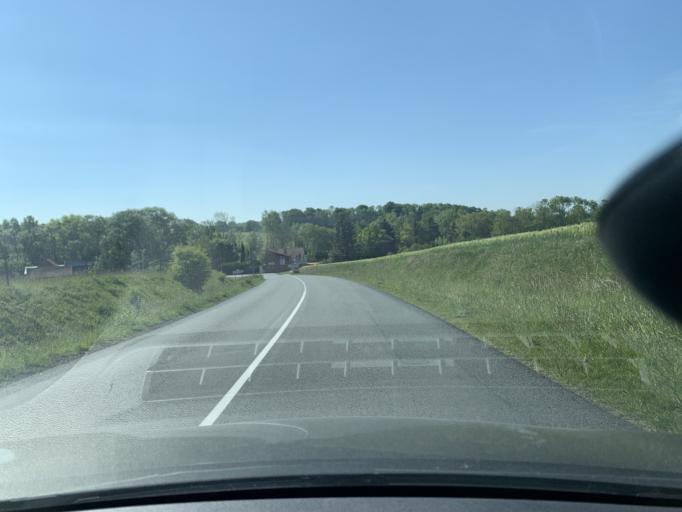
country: FR
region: Nord-Pas-de-Calais
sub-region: Departement du Nord
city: Masnieres
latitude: 50.0790
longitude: 3.2154
